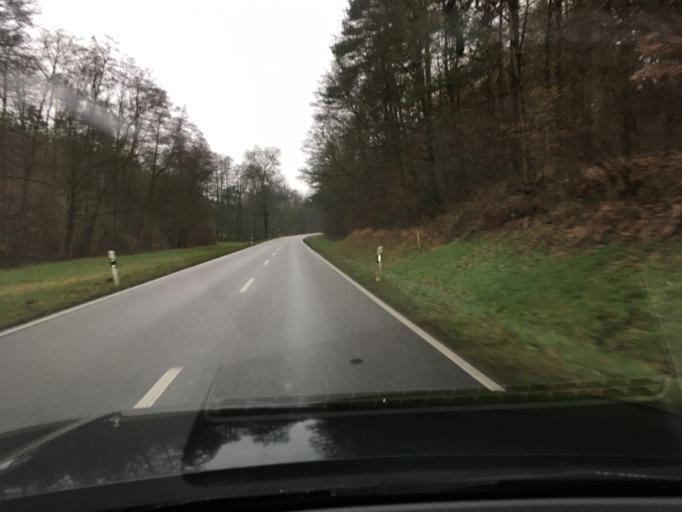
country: DE
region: Baden-Wuerttemberg
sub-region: Karlsruhe Region
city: Konigsbach-Stein
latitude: 48.9559
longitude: 8.5385
